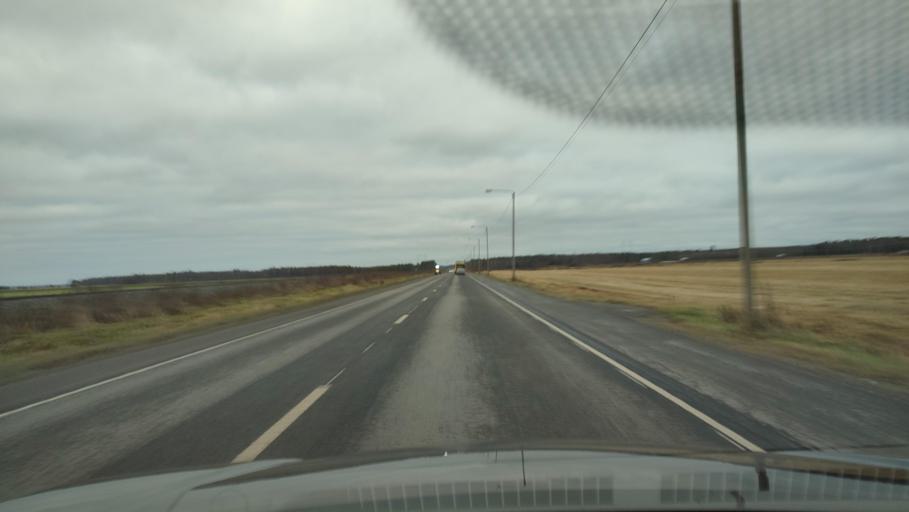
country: FI
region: Southern Ostrobothnia
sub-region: Seinaejoki
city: Ilmajoki
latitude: 62.7401
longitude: 22.6176
